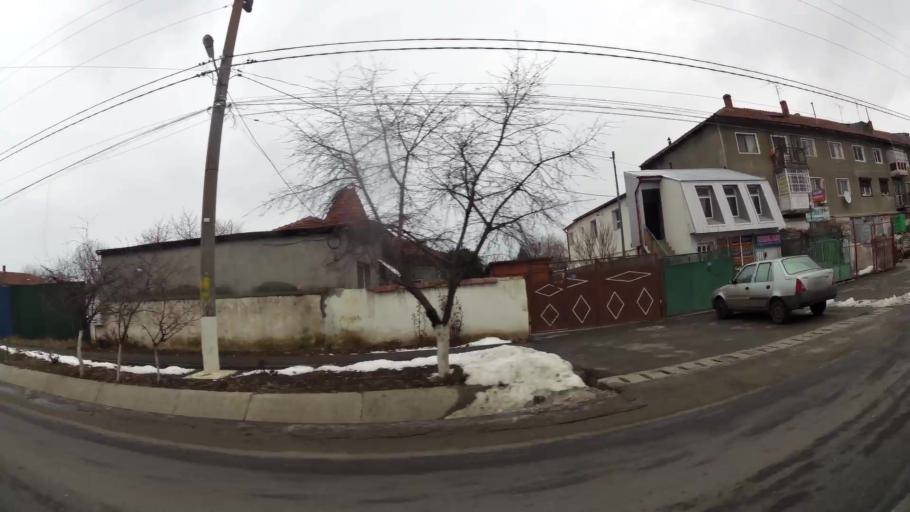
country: RO
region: Ilfov
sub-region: Comuna Afumati
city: Afumati
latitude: 44.5274
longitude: 26.2425
